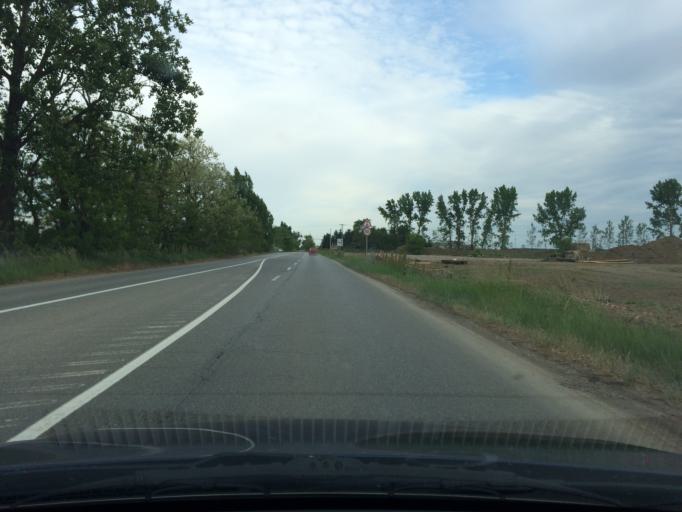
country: HU
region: Szabolcs-Szatmar-Bereg
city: Tiszavasvari
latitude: 47.9336
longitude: 21.3841
